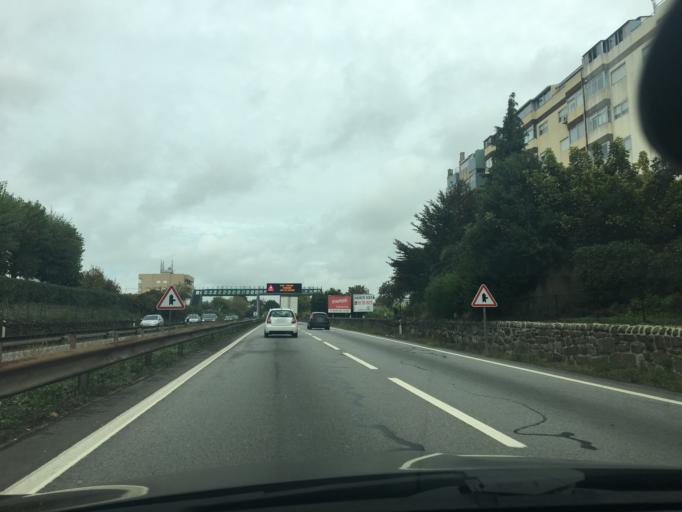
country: PT
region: Porto
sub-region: Matosinhos
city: Sao Mamede de Infesta
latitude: 41.1874
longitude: -8.6254
